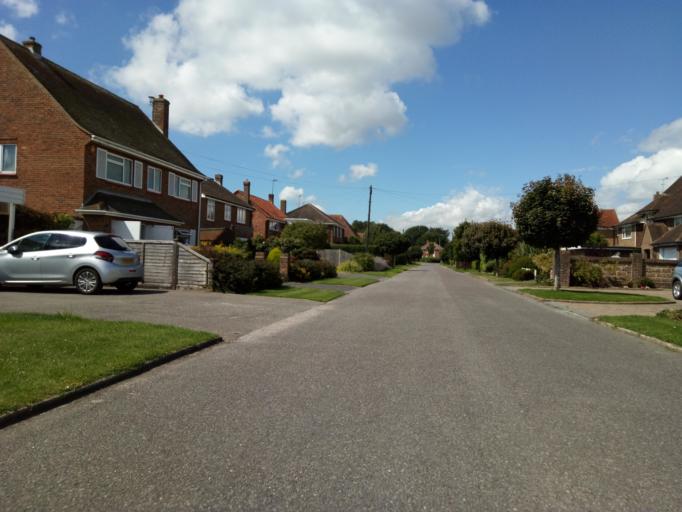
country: GB
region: England
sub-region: West Sussex
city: Barnham
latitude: 50.7907
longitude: -0.6345
